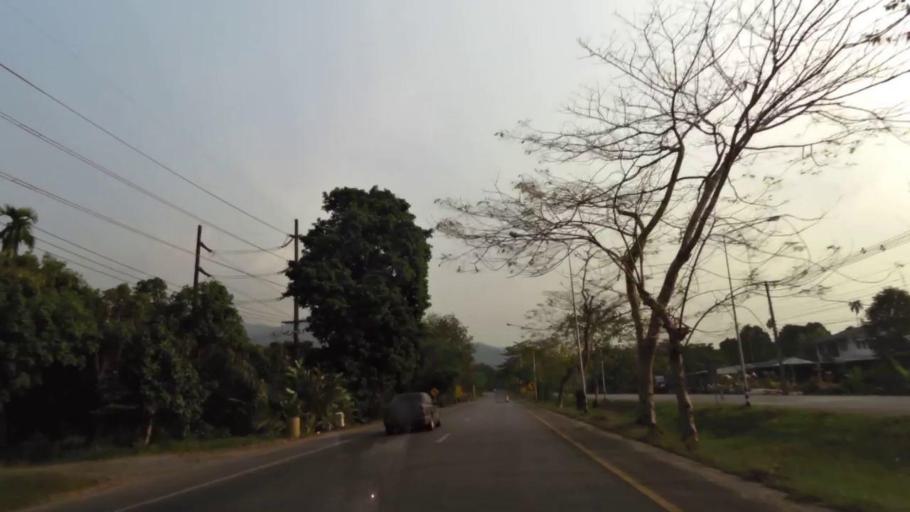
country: TH
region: Chanthaburi
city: Chanthaburi
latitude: 12.5796
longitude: 102.1592
